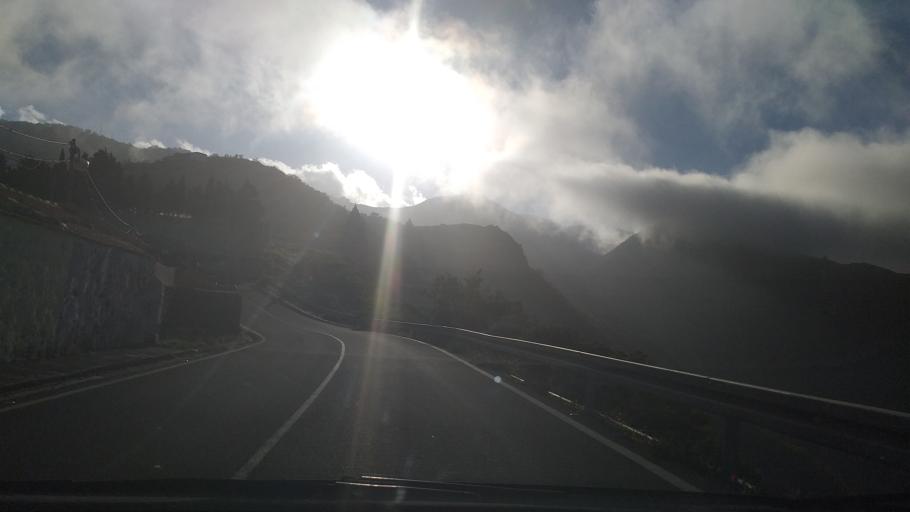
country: ES
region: Canary Islands
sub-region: Provincia de Las Palmas
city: Valsequillo de Gran Canaria
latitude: 27.9569
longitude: -15.5104
